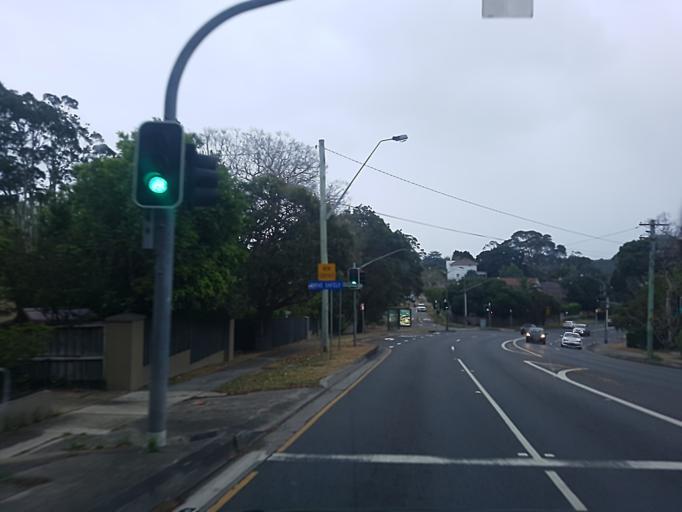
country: AU
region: New South Wales
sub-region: Willoughby
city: Castle Cove
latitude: -33.7922
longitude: 151.2071
